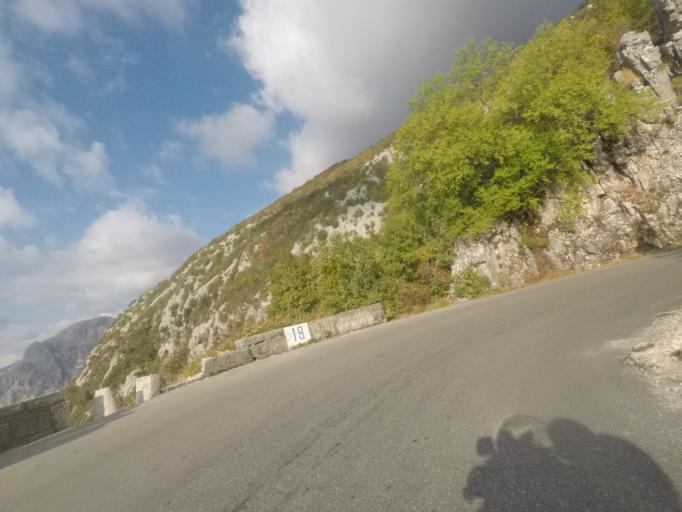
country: ME
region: Kotor
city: Kotor
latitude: 42.4047
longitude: 18.7816
